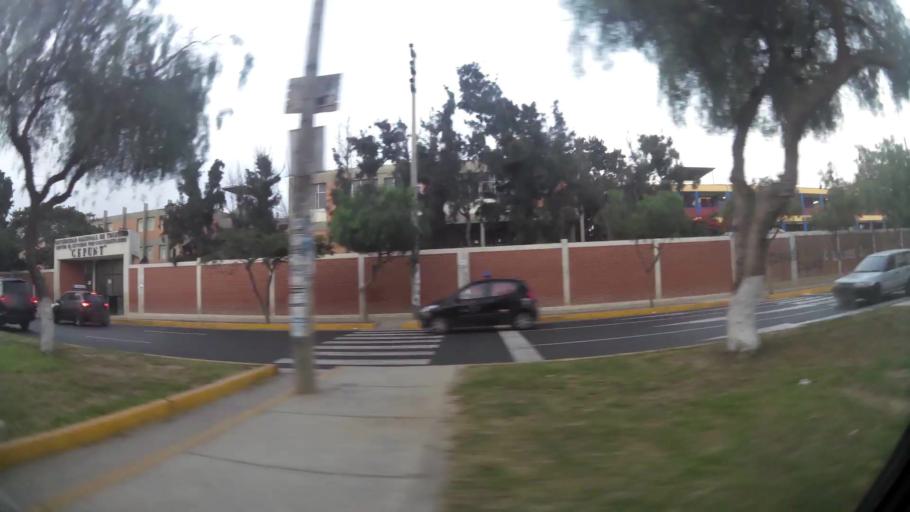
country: PE
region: La Libertad
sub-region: Provincia de Trujillo
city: Trujillo
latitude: -8.1171
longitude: -79.0434
